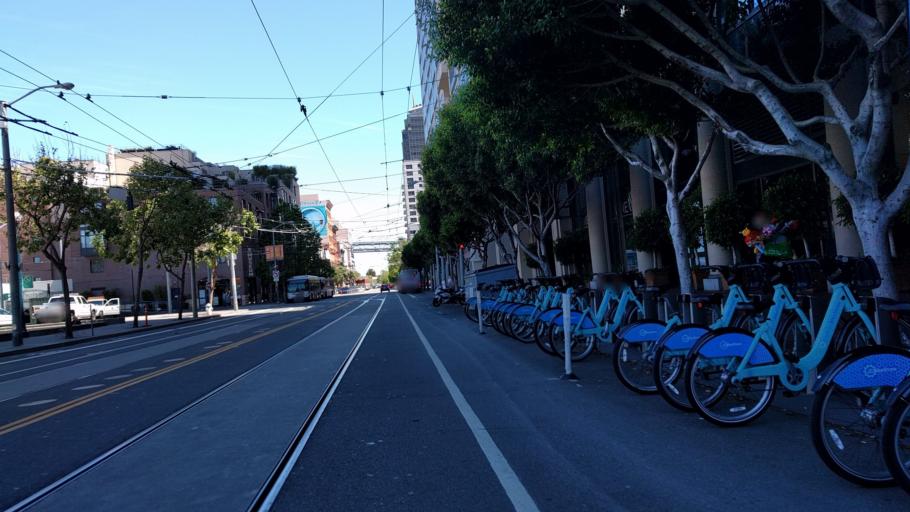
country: US
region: California
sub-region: San Francisco County
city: San Francisco
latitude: 37.7942
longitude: -122.3946
